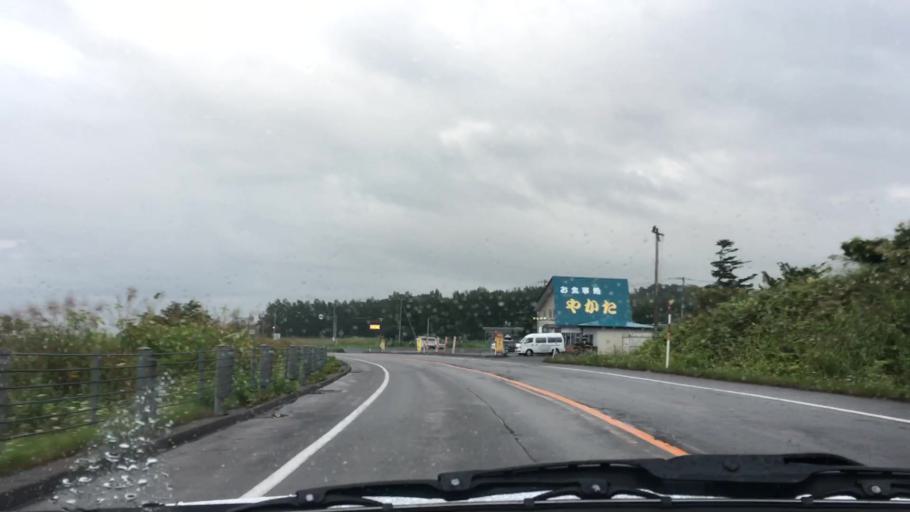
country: JP
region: Hokkaido
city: Nanae
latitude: 42.1793
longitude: 140.4425
